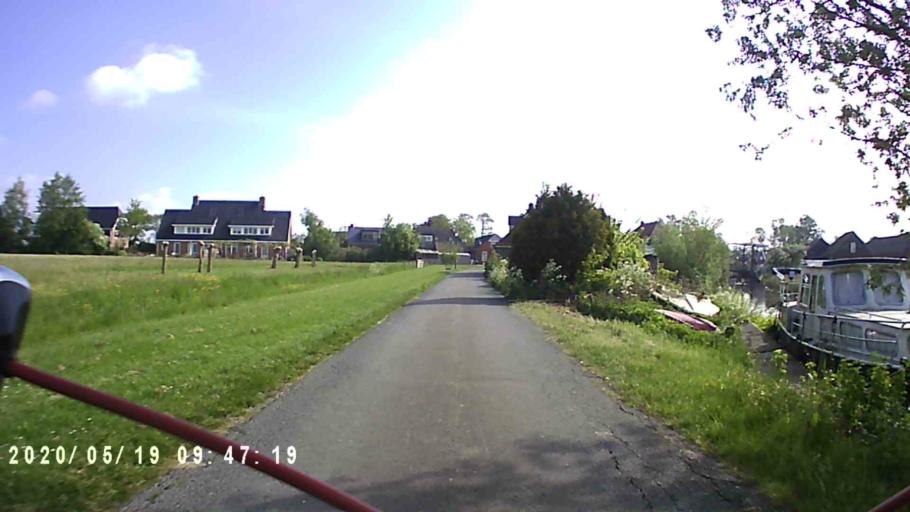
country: NL
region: Groningen
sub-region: Gemeente Zuidhorn
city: Grijpskerk
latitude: 53.2812
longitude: 6.2661
